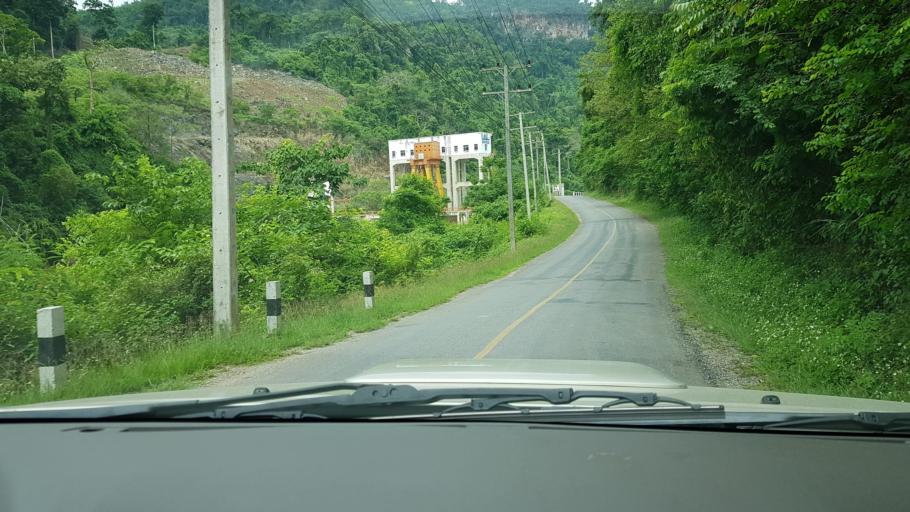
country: TH
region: Nan
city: Chaloem Phra Kiat
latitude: 19.9463
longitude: 101.2427
